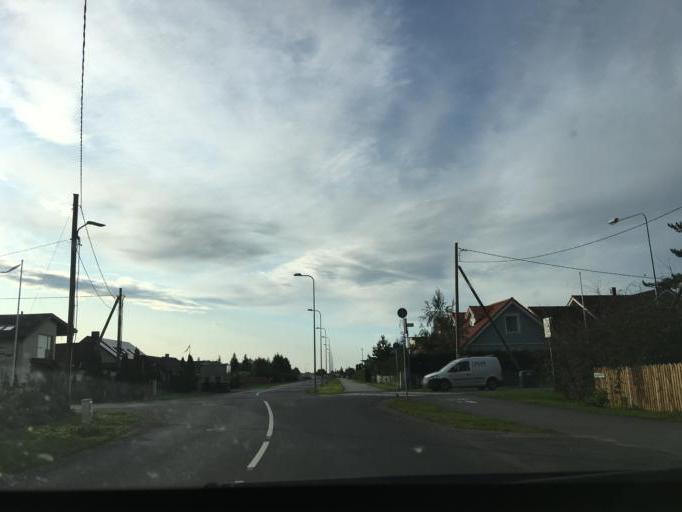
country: EE
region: Harju
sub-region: Tallinna linn
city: Tallinn
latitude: 59.3949
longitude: 24.8141
